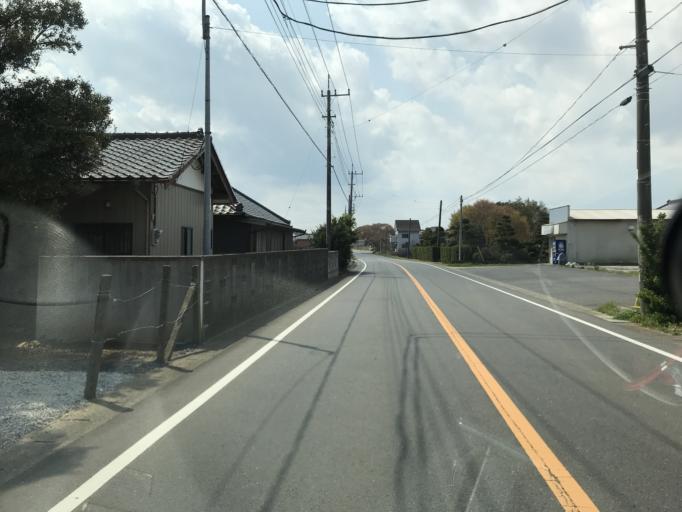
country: JP
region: Chiba
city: Omigawa
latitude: 35.8665
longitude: 140.5654
